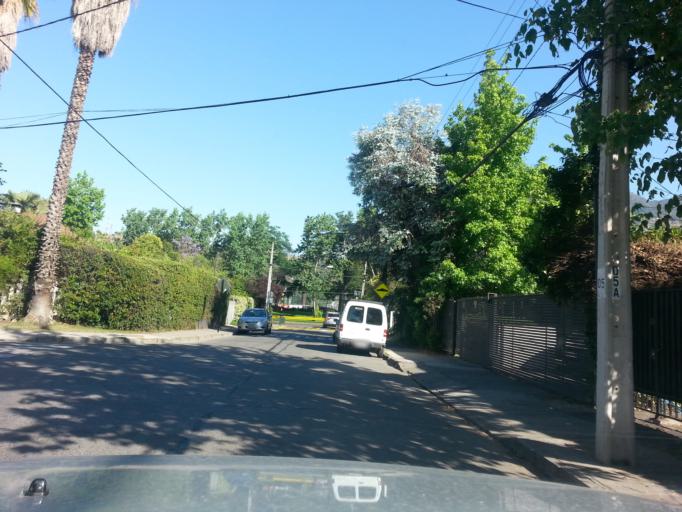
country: CL
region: Santiago Metropolitan
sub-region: Provincia de Santiago
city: Villa Presidente Frei, Nunoa, Santiago, Chile
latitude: -33.3875
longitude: -70.5922
